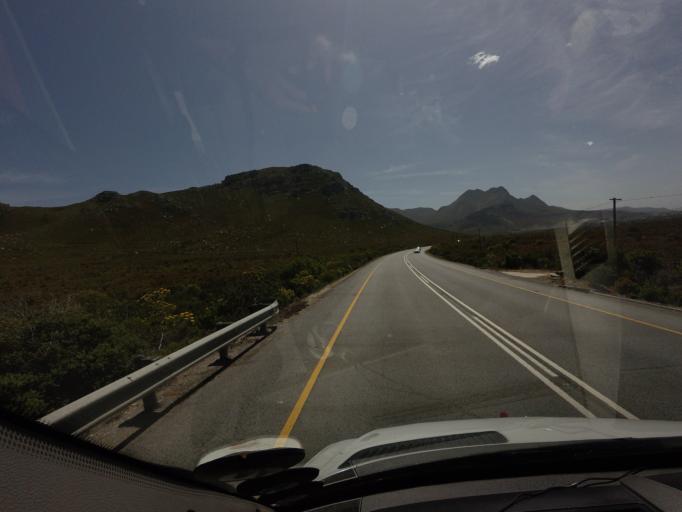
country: ZA
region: Western Cape
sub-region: Overberg District Municipality
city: Grabouw
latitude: -34.3469
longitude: 18.9761
